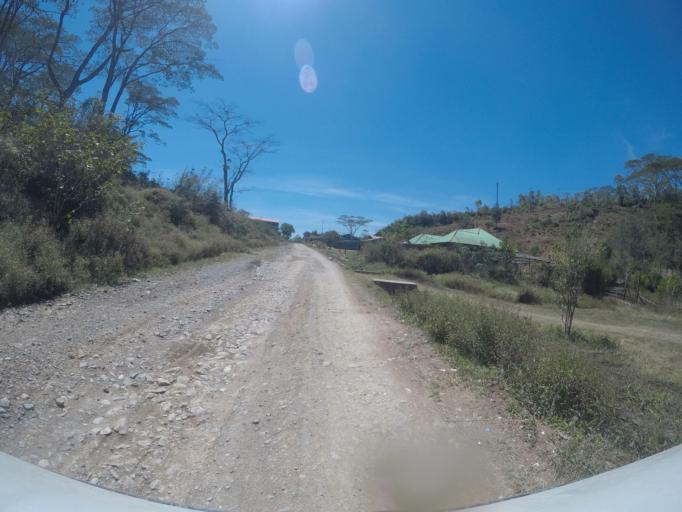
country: TL
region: Ermera
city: Gleno
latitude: -8.7743
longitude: 125.3963
